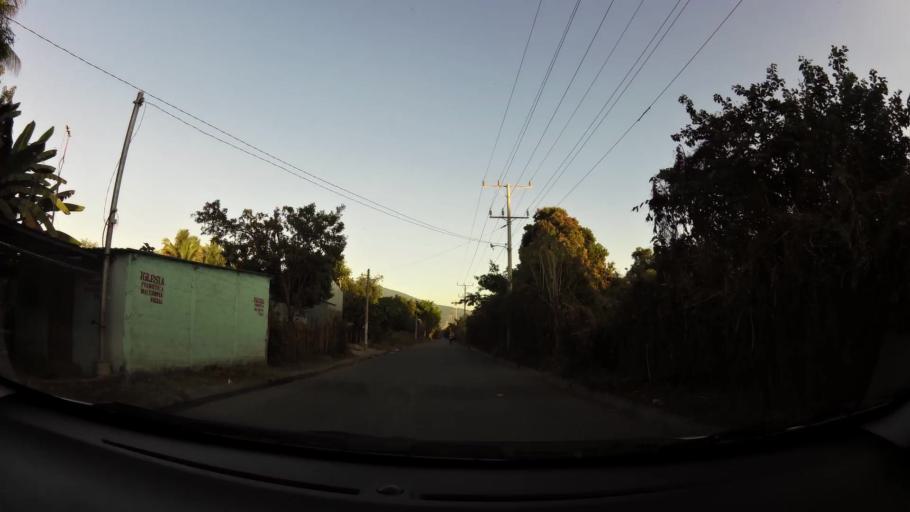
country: SV
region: Sonsonate
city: Armenia
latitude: 13.7407
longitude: -89.3951
